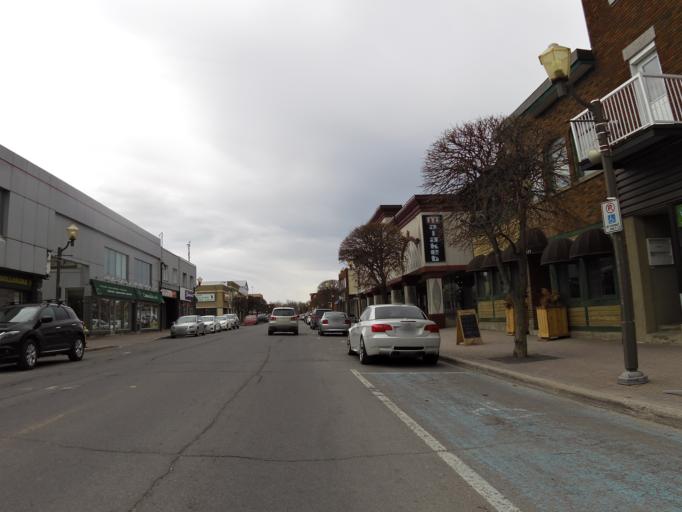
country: CA
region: Ontario
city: Hawkesbury
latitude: 45.6100
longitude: -74.6080
